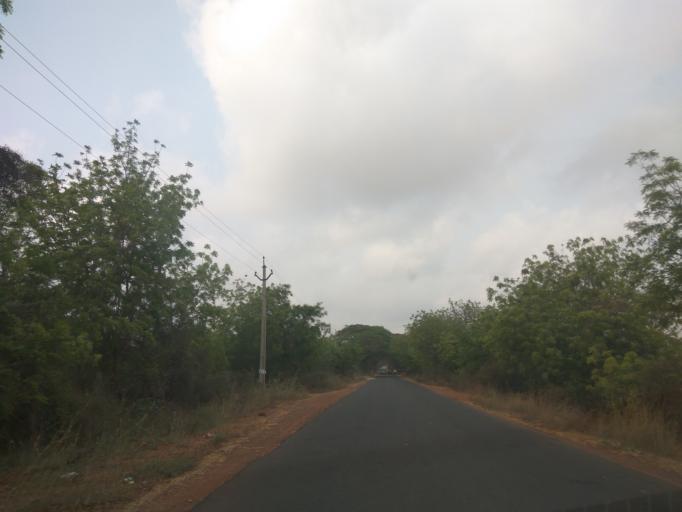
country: IN
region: Andhra Pradesh
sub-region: Prakasam
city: Kandukur
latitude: 15.2073
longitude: 79.8656
